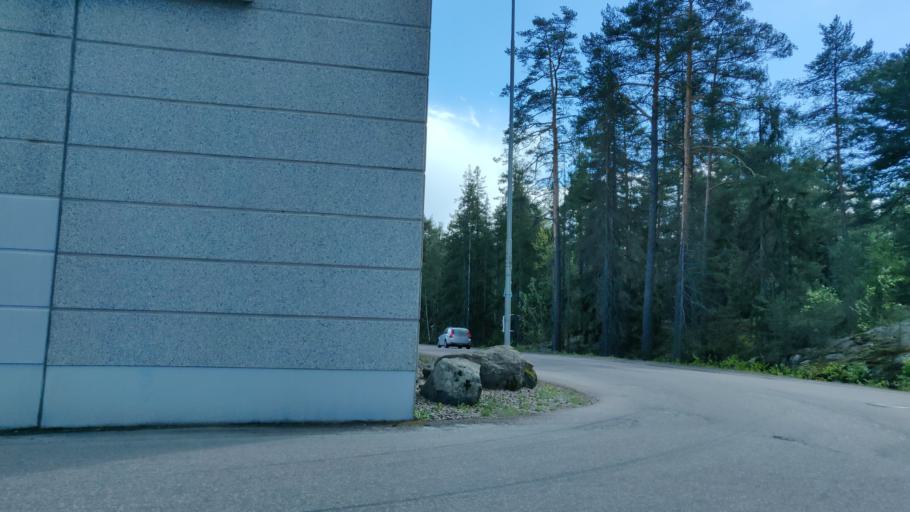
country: SE
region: Vaermland
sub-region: Hammaro Kommun
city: Skoghall
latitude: 59.3757
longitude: 13.4381
